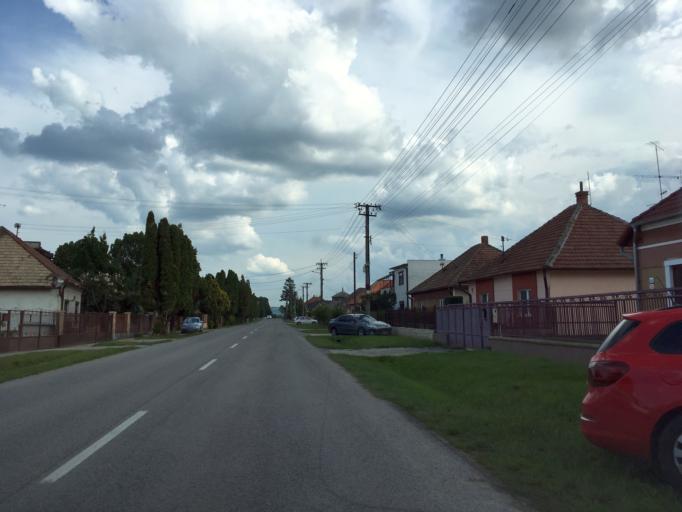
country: HU
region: Komarom-Esztergom
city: Dunaalmas
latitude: 47.7850
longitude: 18.2936
